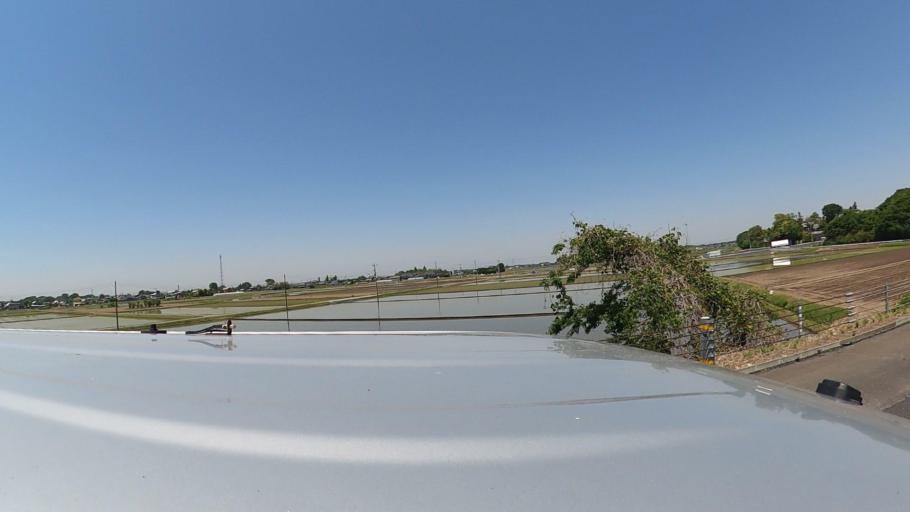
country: JP
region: Ibaraki
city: Mitsukaido
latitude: 35.9907
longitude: 140.0283
